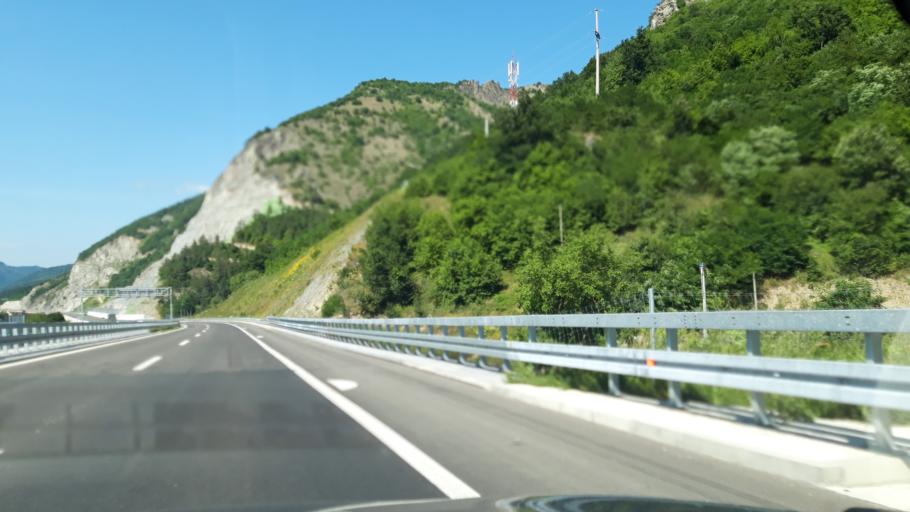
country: RS
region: Central Serbia
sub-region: Pcinjski Okrug
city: Vladicin Han
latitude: 42.7485
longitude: 22.0815
